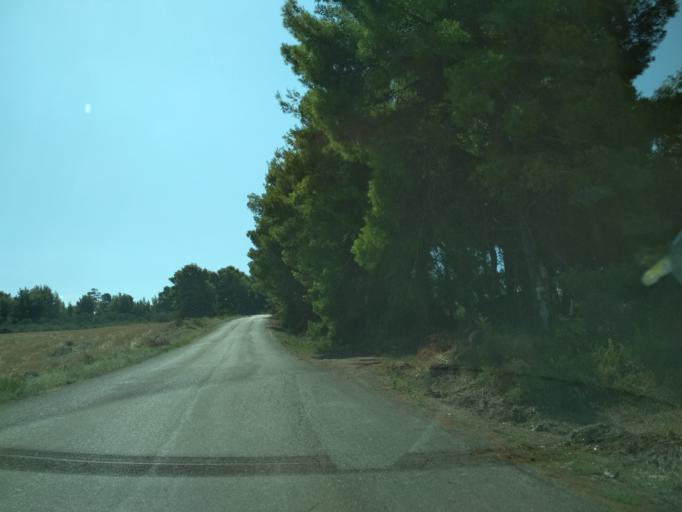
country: GR
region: Central Greece
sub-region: Nomos Evvoias
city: Roviai
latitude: 38.8229
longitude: 23.2309
